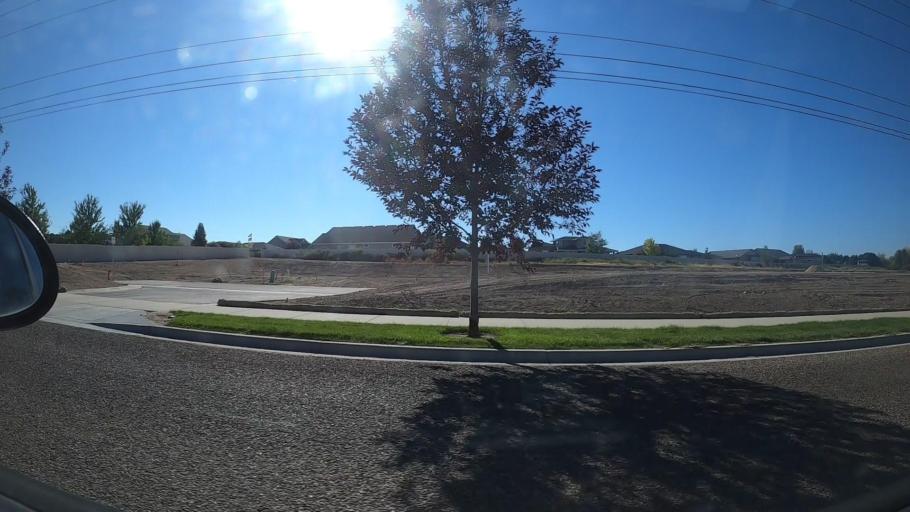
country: US
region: Idaho
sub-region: Canyon County
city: Nampa
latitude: 43.5524
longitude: -116.6127
